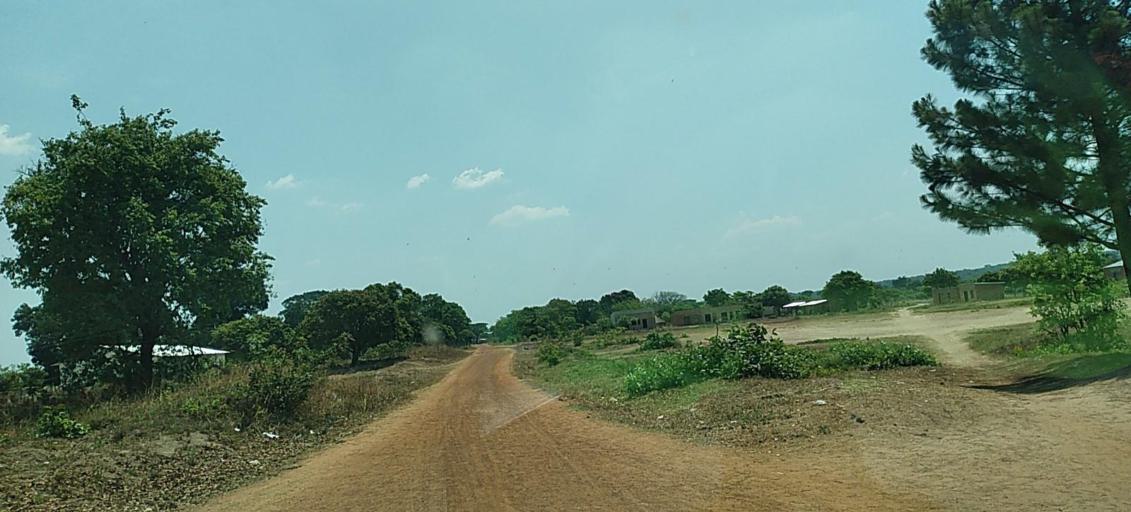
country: CD
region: Katanga
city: Kolwezi
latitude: -11.2972
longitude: 25.2160
